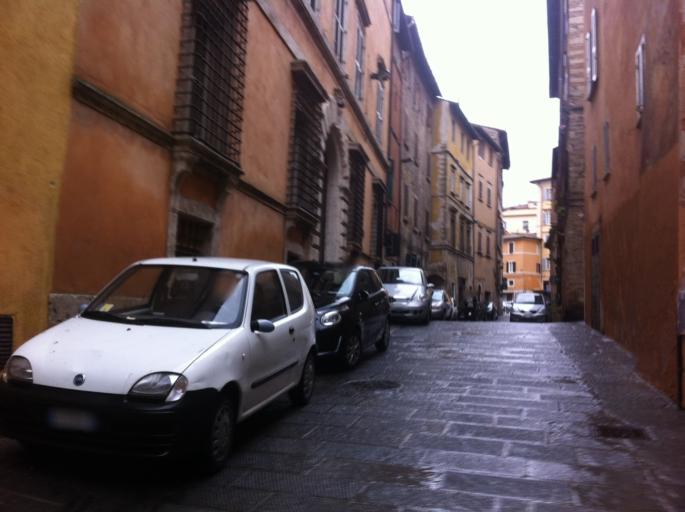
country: IT
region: Umbria
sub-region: Provincia di Perugia
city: Perugia
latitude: 43.1126
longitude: 12.3916
